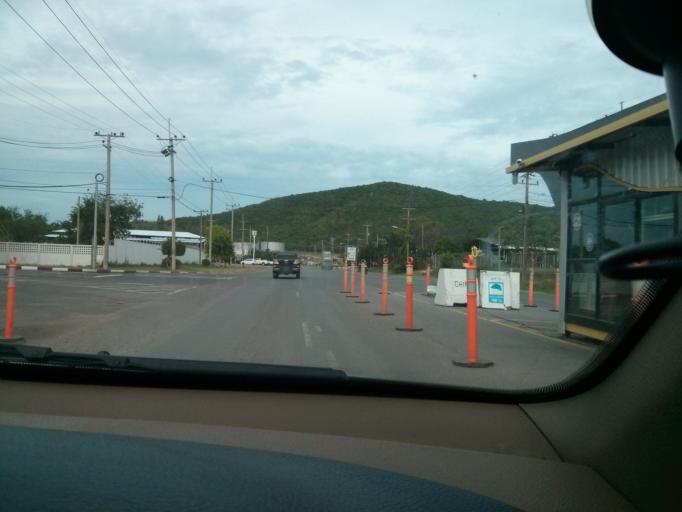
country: TH
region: Chon Buri
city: Sattahip
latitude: 12.6234
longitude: 100.9290
